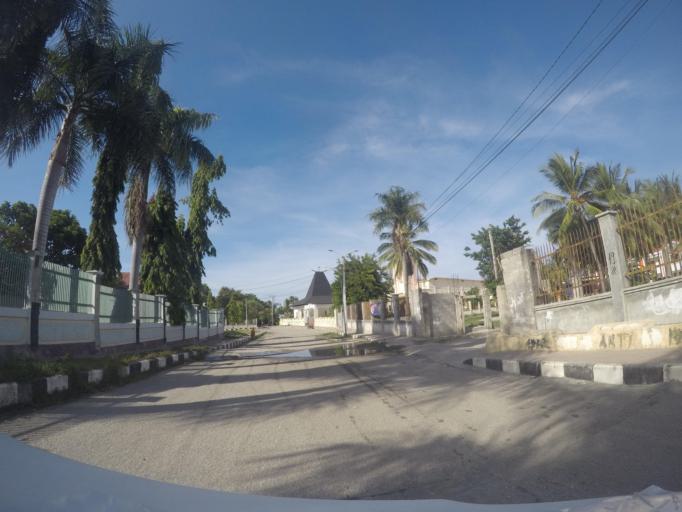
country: TL
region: Baucau
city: Baucau
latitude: -8.4626
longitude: 126.4533
